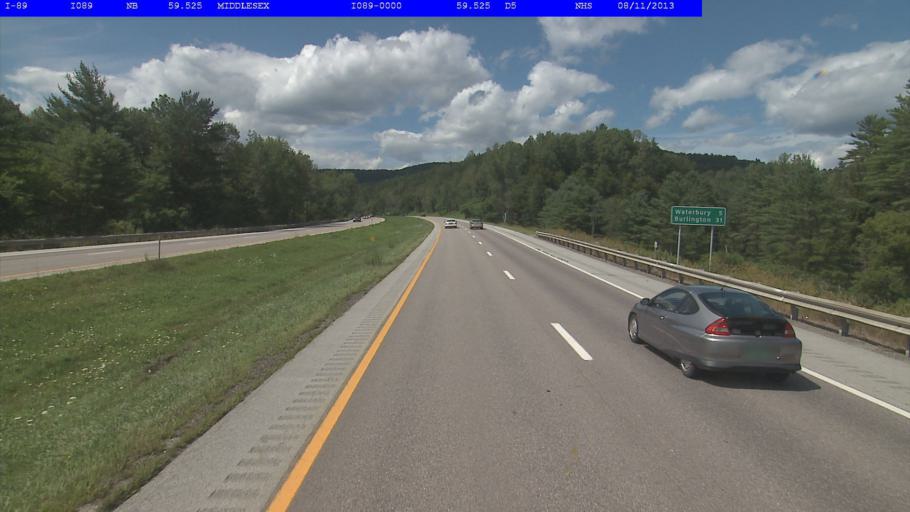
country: US
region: Vermont
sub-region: Washington County
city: Waterbury
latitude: 44.3086
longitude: -72.6924
